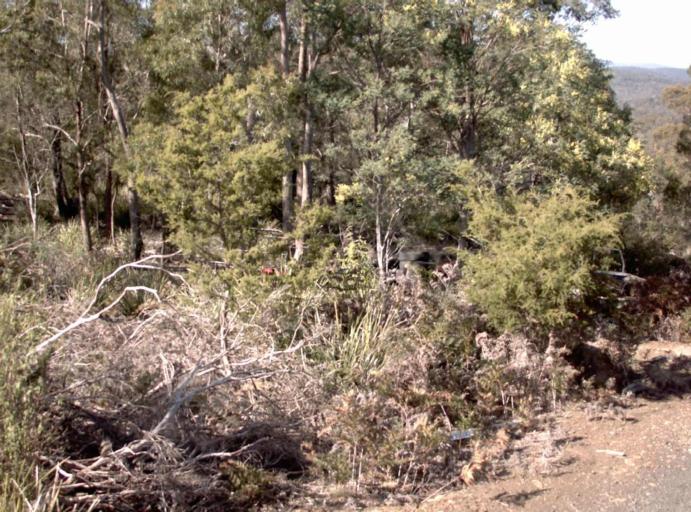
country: AU
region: Tasmania
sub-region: Launceston
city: Mayfield
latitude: -41.3179
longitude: 147.1190
